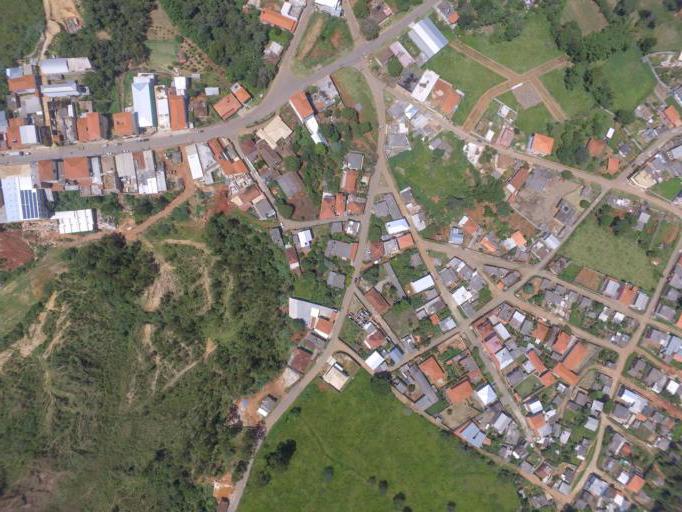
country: BR
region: Minas Gerais
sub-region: Tiradentes
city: Tiradentes
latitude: -21.0527
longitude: -44.0885
